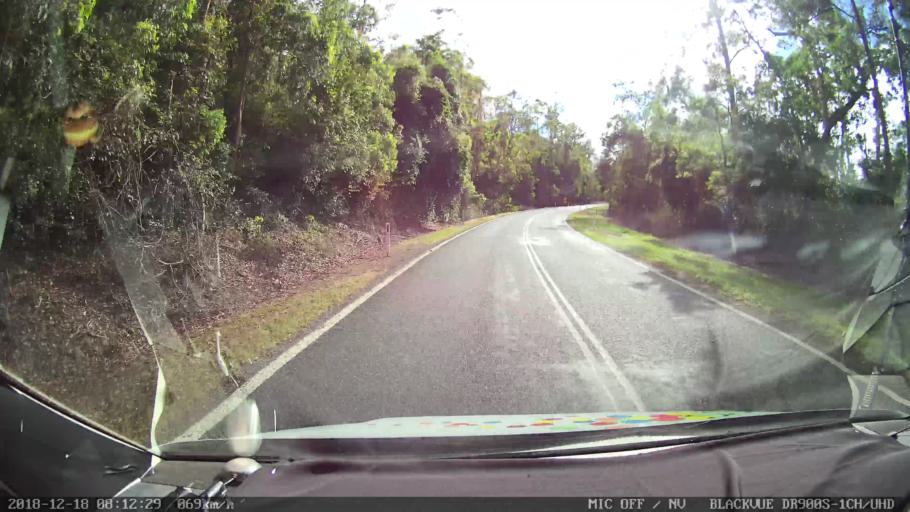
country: AU
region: New South Wales
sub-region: Kyogle
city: Kyogle
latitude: -28.3393
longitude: 152.6711
